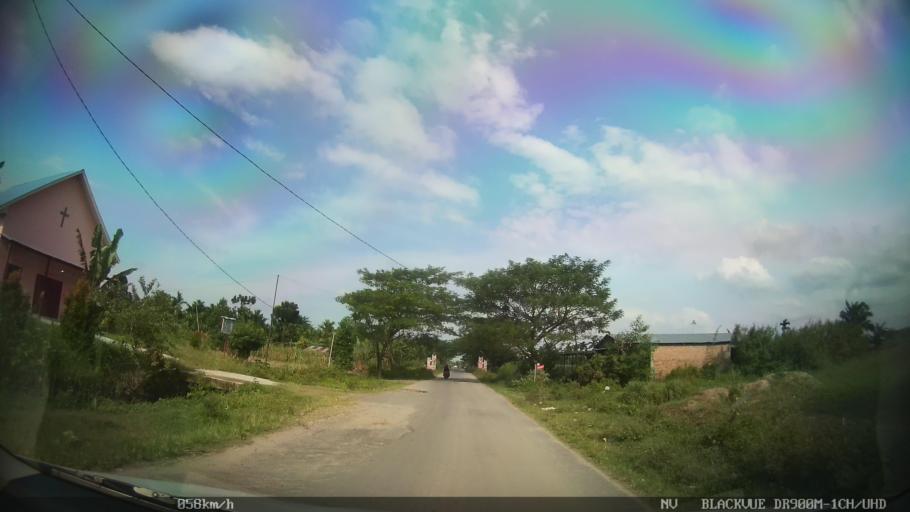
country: ID
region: North Sumatra
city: Medan
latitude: 3.5730
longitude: 98.7711
